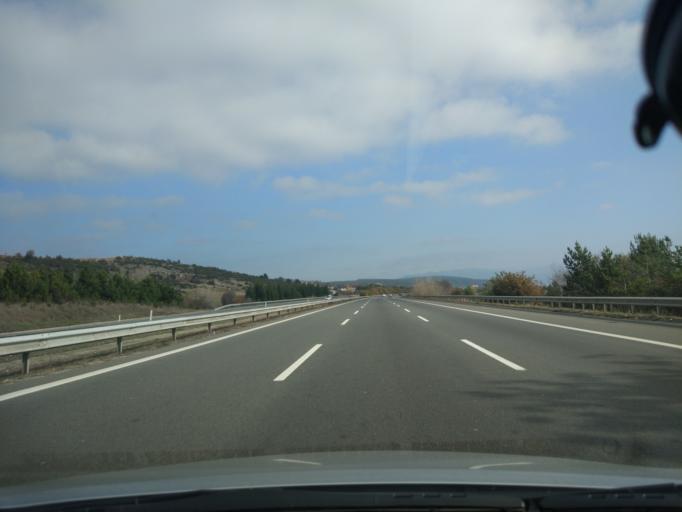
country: TR
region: Bolu
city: Bolu
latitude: 40.7753
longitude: 31.6852
